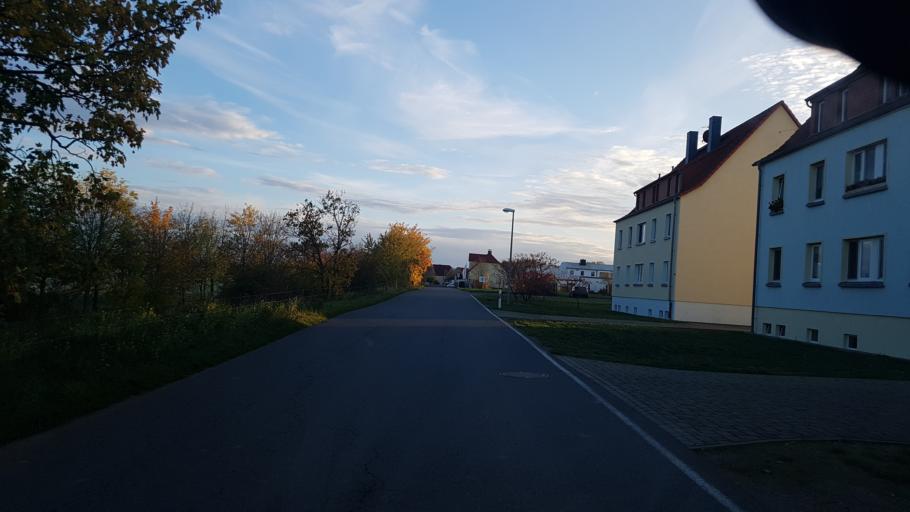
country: DE
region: Saxony
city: Belgern
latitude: 51.4632
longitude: 13.1652
